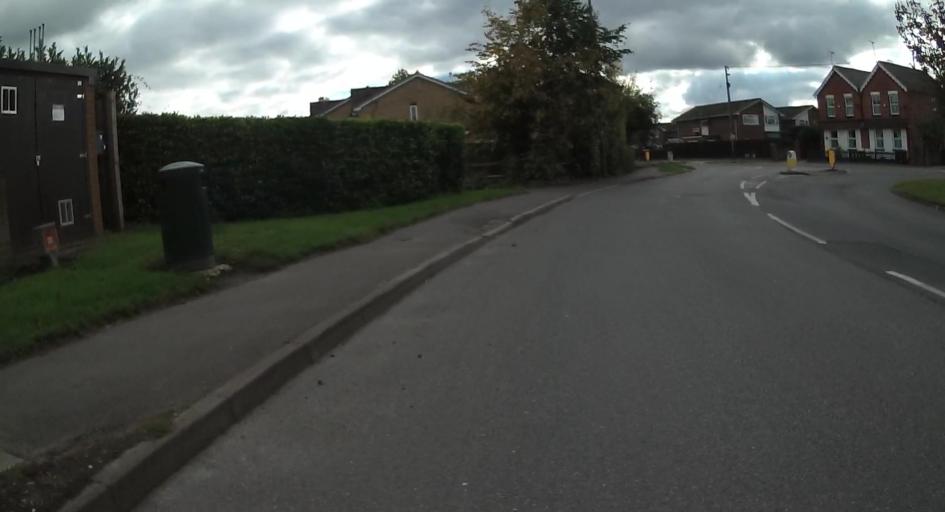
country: GB
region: England
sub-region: Surrey
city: Seale
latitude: 51.2358
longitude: -0.7315
